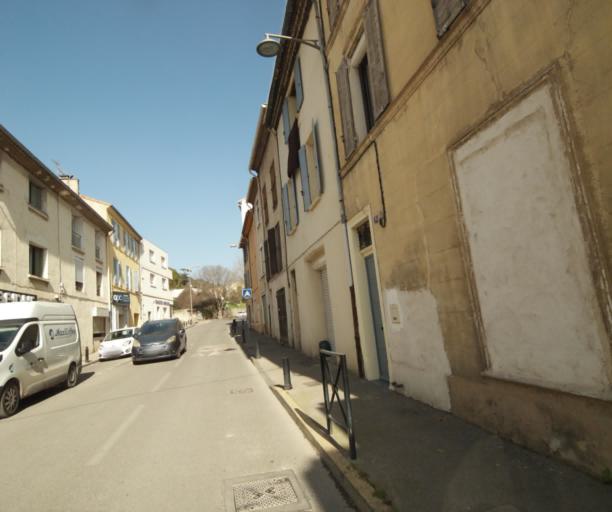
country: FR
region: Provence-Alpes-Cote d'Azur
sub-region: Departement des Bouches-du-Rhone
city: Gardanne
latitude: 43.4574
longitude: 5.4724
